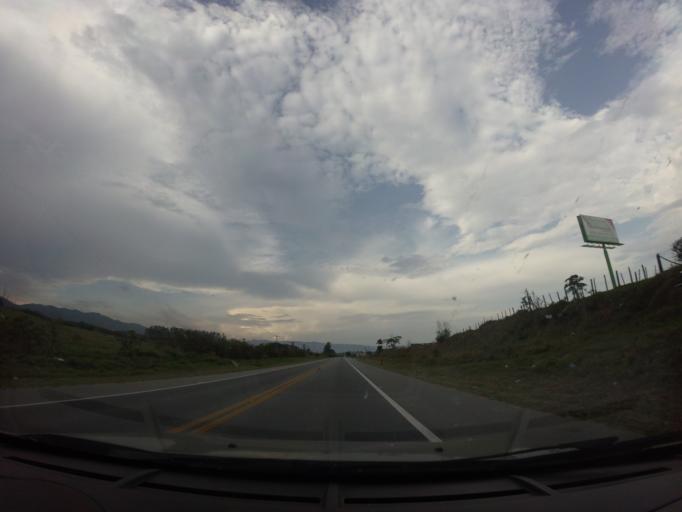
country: BR
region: Sao Paulo
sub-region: Tremembe
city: Tremembe
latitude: -22.9749
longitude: -45.6452
